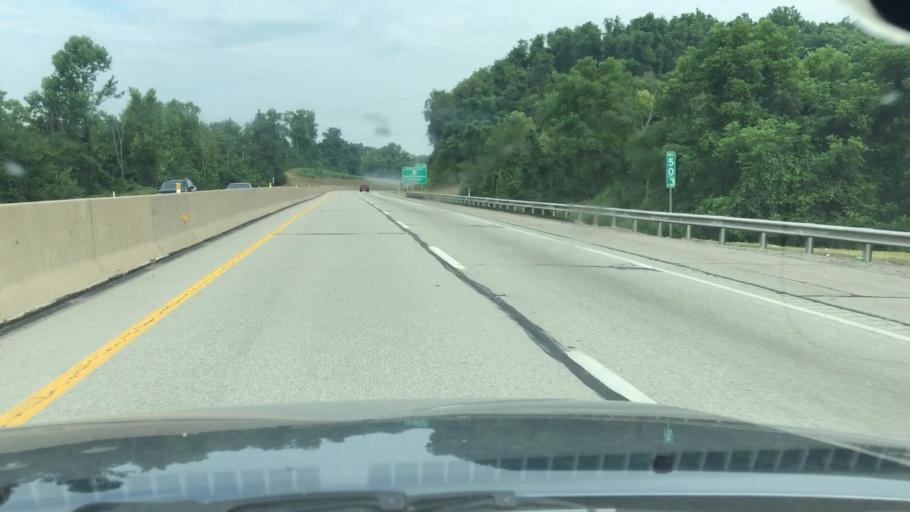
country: US
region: Pennsylvania
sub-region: Allegheny County
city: Cheswick
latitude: 40.5153
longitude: -79.7978
